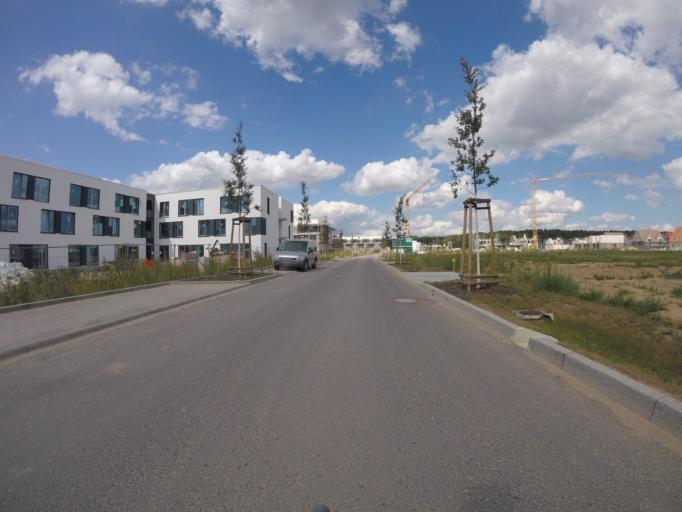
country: DE
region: Brandenburg
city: Werder
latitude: 52.4142
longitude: 12.9793
